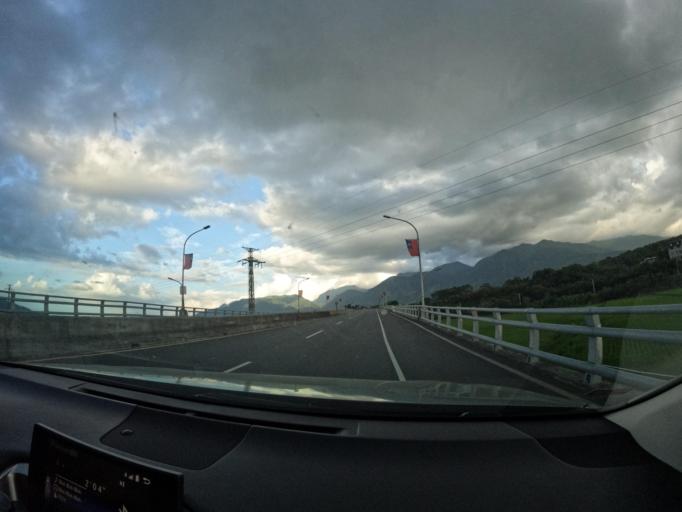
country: TW
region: Taiwan
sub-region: Taitung
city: Taitung
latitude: 23.1843
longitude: 121.2497
